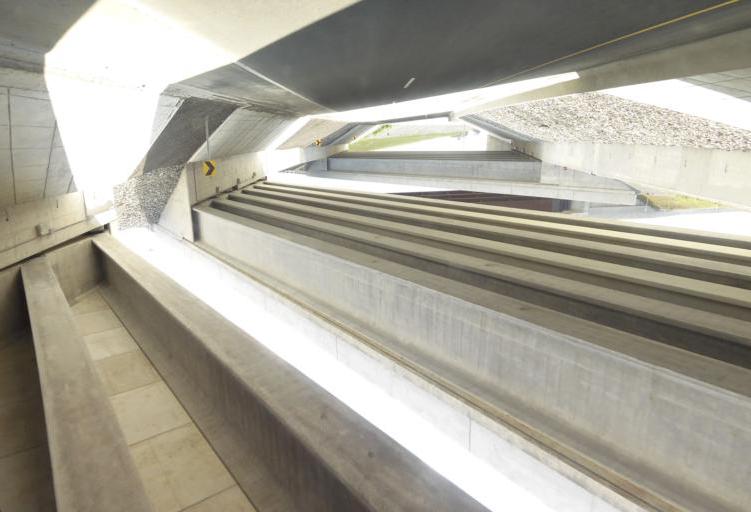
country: CA
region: Ontario
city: Ajax
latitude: 43.9514
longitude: -79.0084
